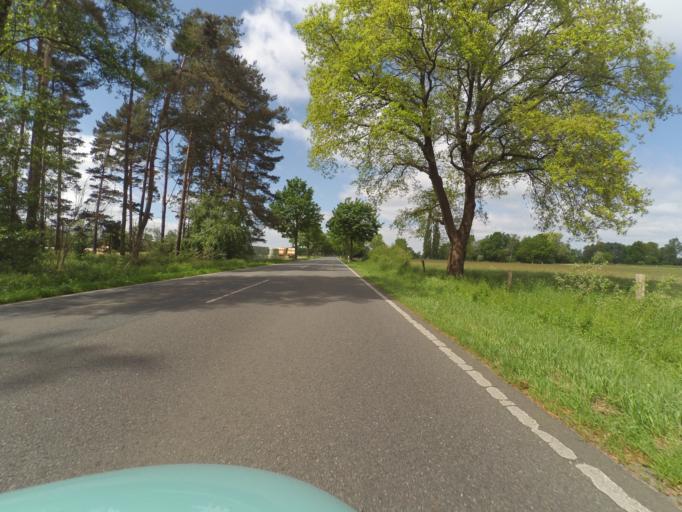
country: DE
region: Lower Saxony
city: Ribbesbuttel
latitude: 52.4337
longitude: 10.4815
